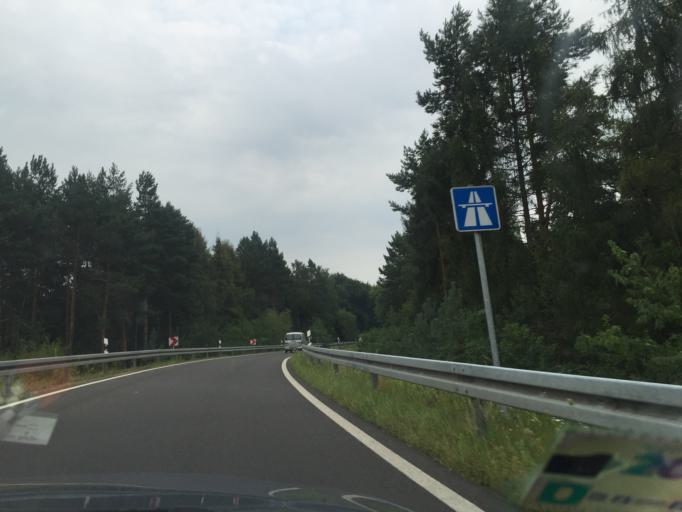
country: DE
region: Brandenburg
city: Bernau bei Berlin
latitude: 52.7285
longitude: 13.5385
